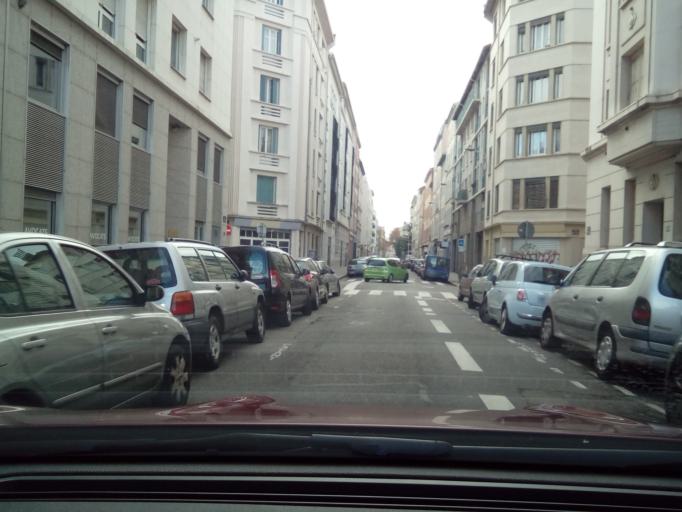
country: FR
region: Rhone-Alpes
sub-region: Departement du Rhone
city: Lyon
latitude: 45.7583
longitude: 4.8493
